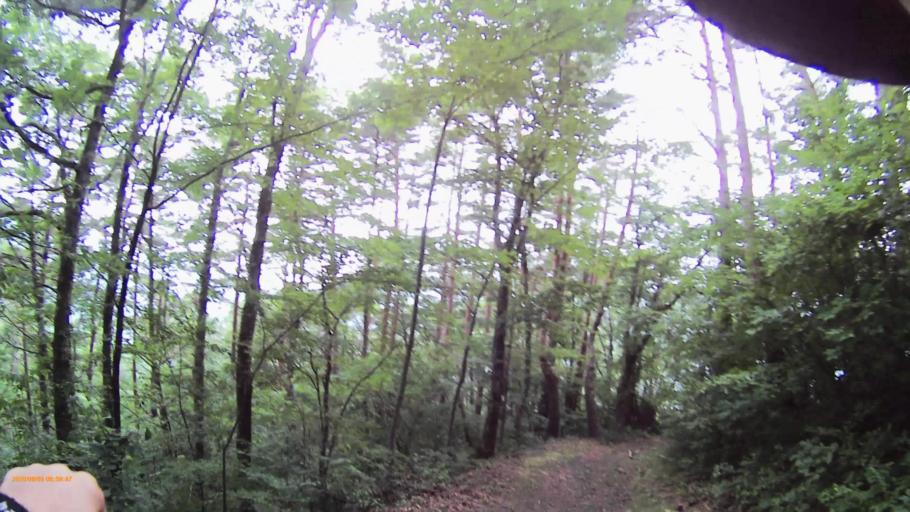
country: JP
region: Nagano
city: Ina
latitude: 35.9482
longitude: 137.7901
